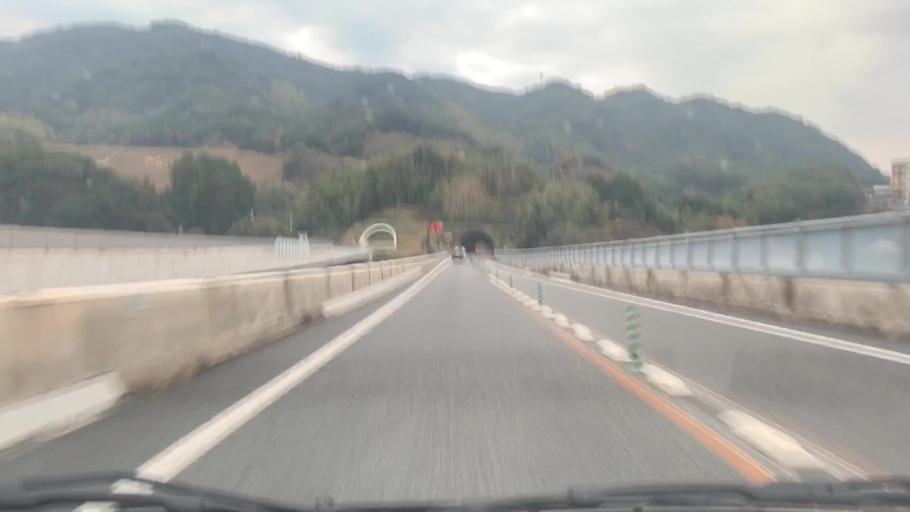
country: JP
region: Nagasaki
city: Obita
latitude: 32.8008
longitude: 129.9651
